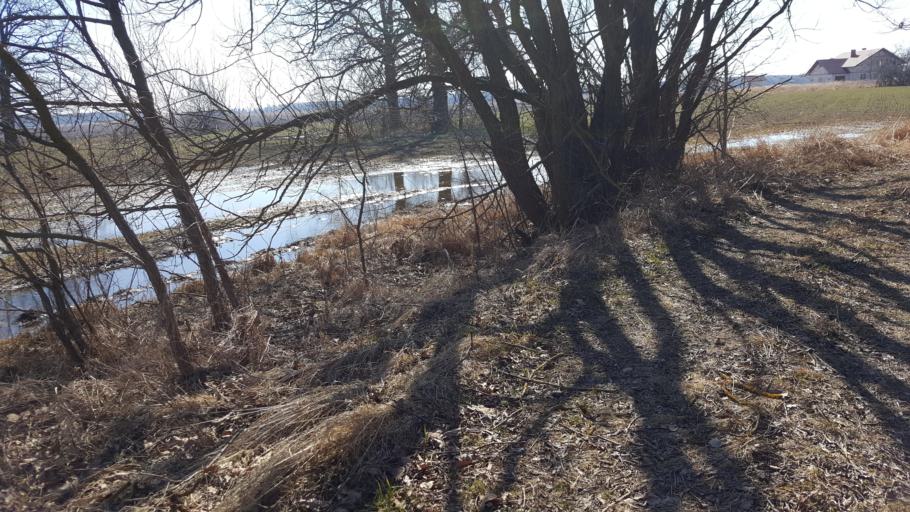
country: BY
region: Brest
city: Kamyanyets
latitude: 52.3629
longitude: 23.7651
